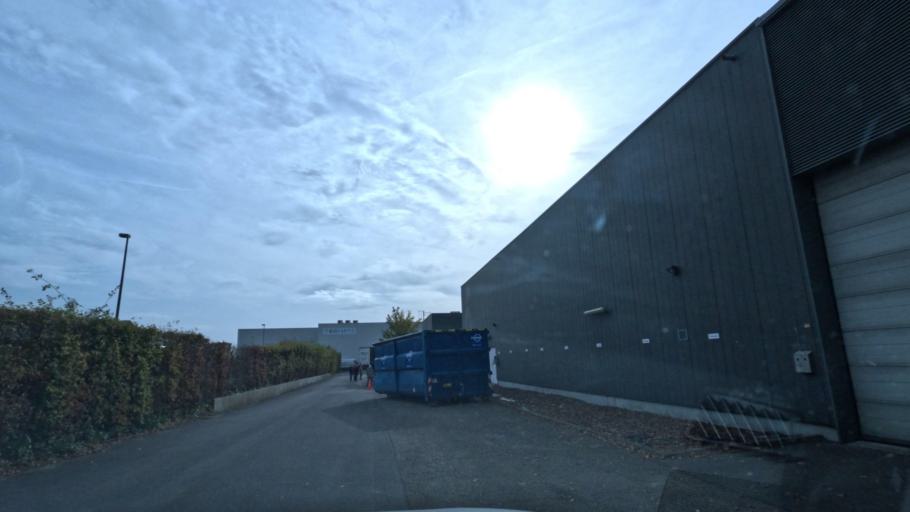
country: BE
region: Flanders
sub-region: Provincie Antwerpen
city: Mechelen
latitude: 51.0563
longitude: 4.4536
